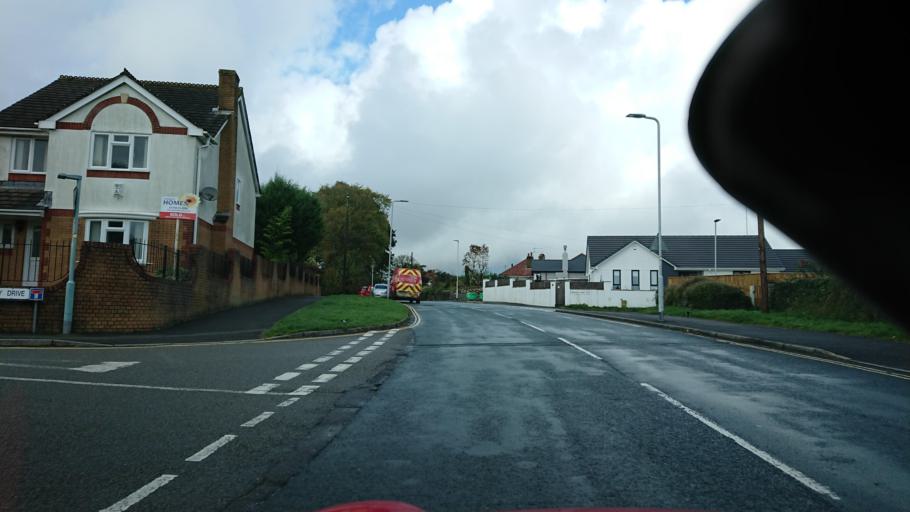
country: GB
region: England
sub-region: Plymouth
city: Plymouth
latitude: 50.4054
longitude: -4.1270
